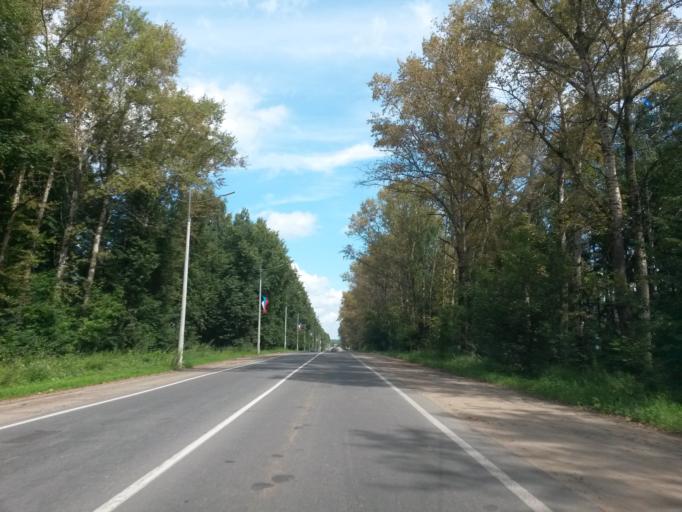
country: RU
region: Jaroslavl
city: Pereslavl'-Zalesskiy
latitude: 56.7544
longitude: 38.8647
